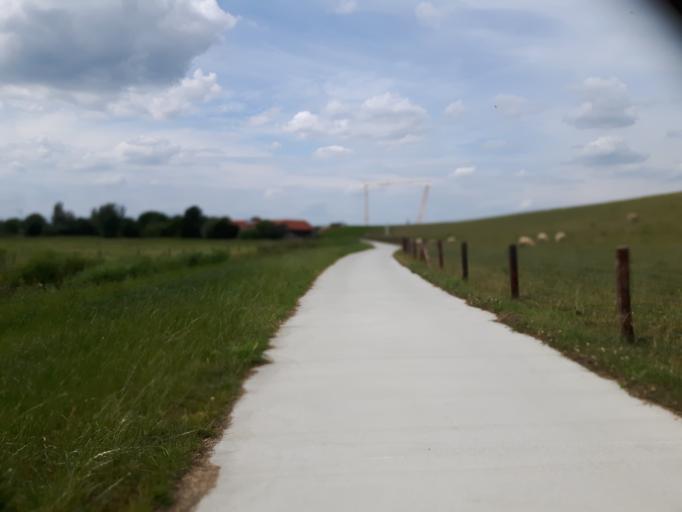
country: DE
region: Lower Saxony
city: Varel
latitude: 53.3905
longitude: 8.2139
